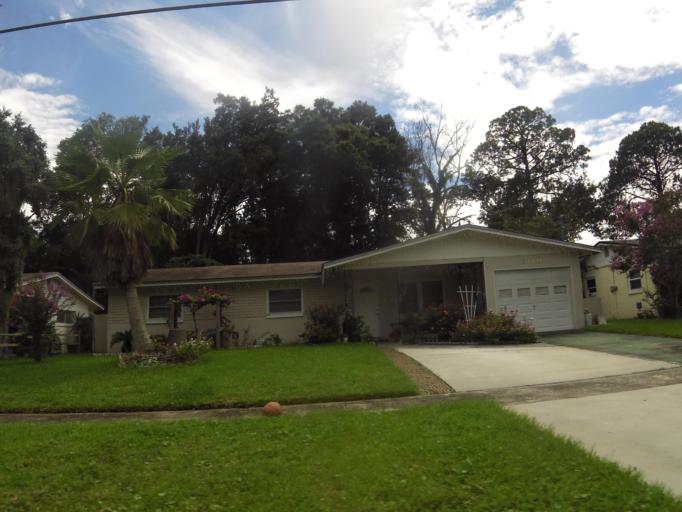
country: US
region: Florida
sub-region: Duval County
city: Jacksonville
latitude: 30.2683
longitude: -81.6066
